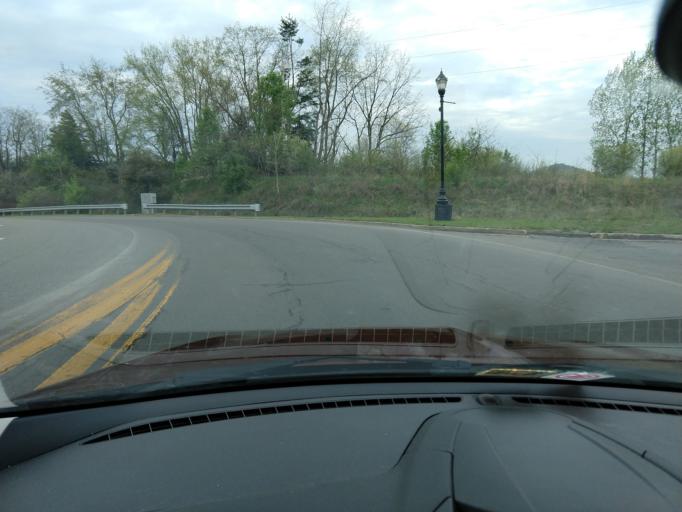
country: US
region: West Virginia
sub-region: Harrison County
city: Bridgeport
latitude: 39.3150
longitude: -80.2743
